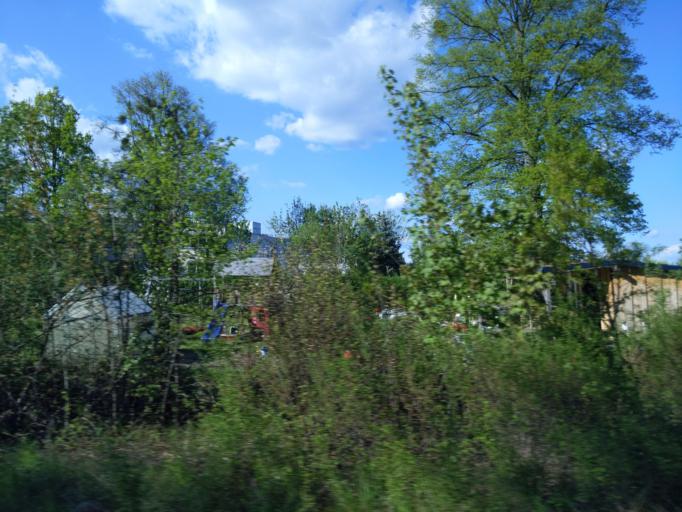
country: DE
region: Saxony
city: Ottendorf-Okrilla
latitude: 51.1275
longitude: 13.8371
